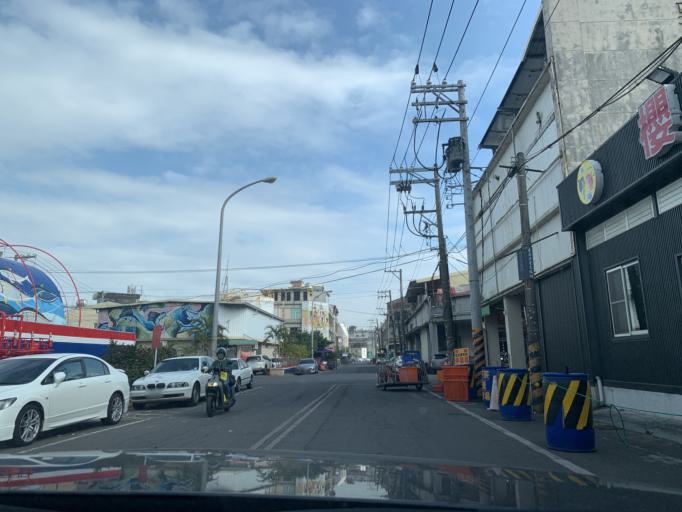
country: TW
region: Taiwan
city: Fengshan
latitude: 22.4672
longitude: 120.4439
